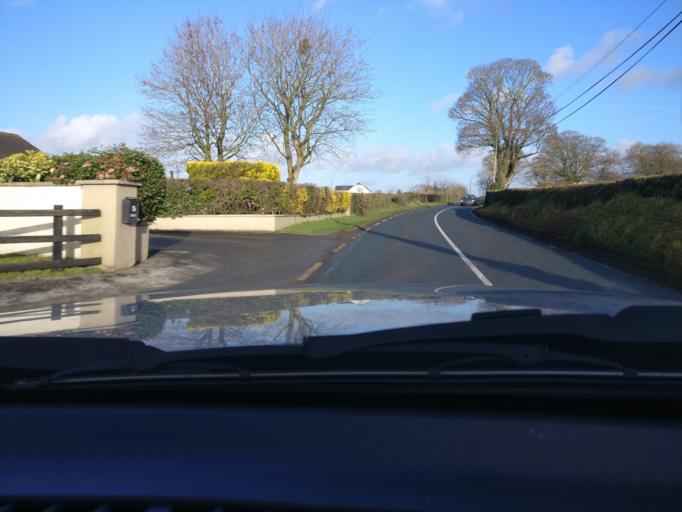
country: IE
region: Leinster
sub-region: Uibh Fhaili
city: Clara
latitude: 53.4059
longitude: -7.5744
